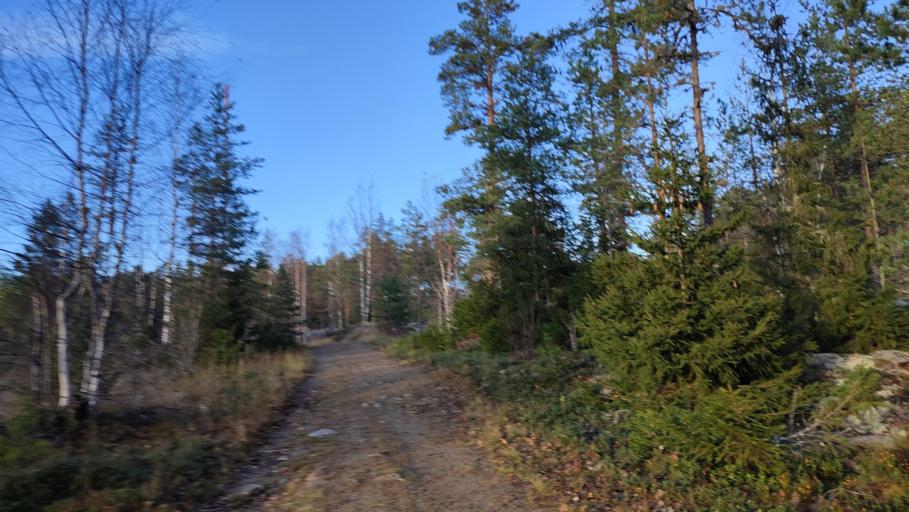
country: FI
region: Southern Ostrobothnia
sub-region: Suupohja
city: Karijoki
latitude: 62.2821
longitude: 21.6437
